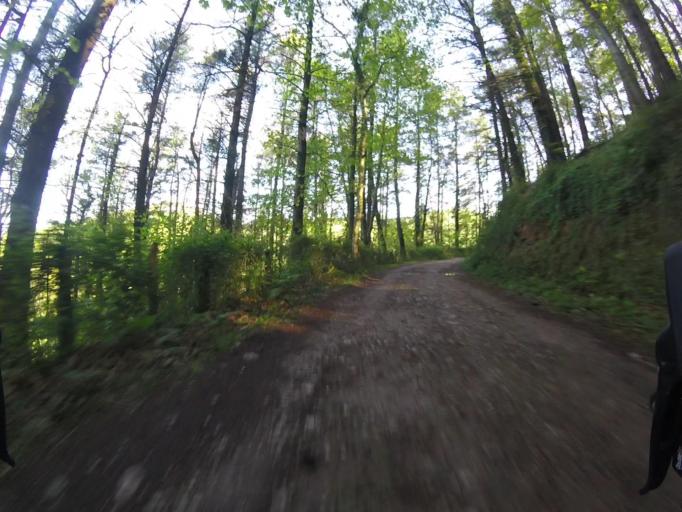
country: ES
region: Basque Country
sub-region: Provincia de Guipuzcoa
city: Andoain
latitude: 43.2105
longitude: -1.9901
